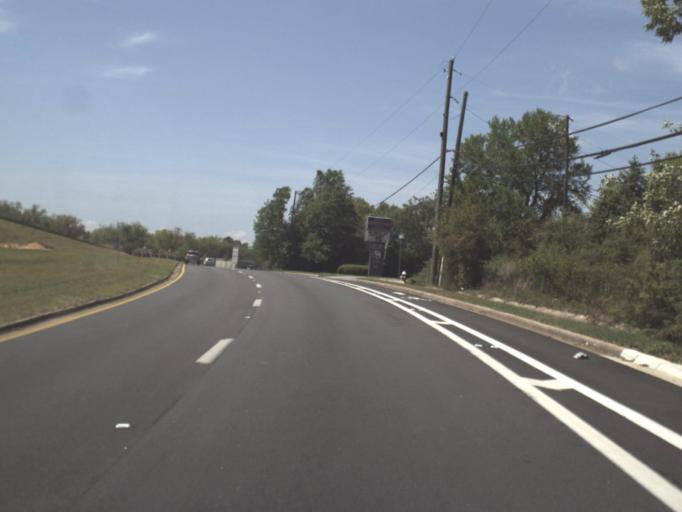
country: US
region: Florida
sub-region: Escambia County
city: Ferry Pass
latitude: 30.5348
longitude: -87.2052
